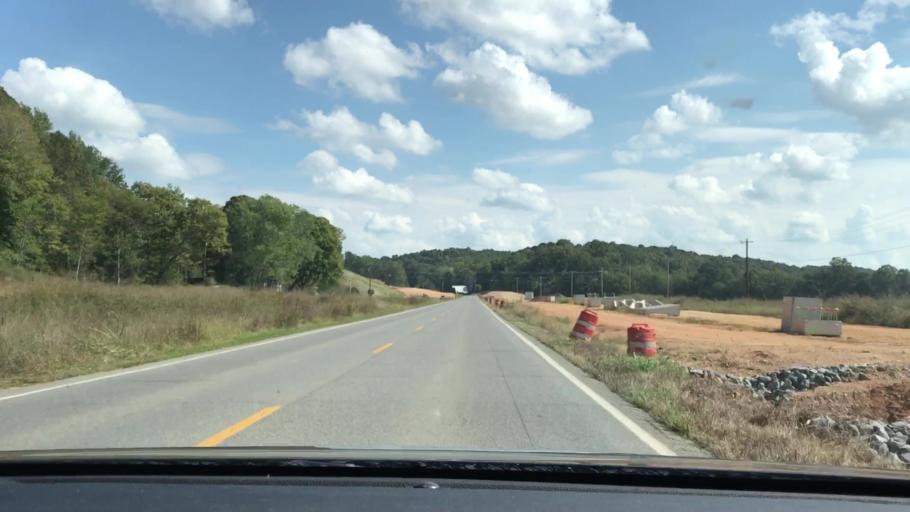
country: US
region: Kentucky
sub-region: Trigg County
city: Cadiz
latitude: 36.8052
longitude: -87.9158
